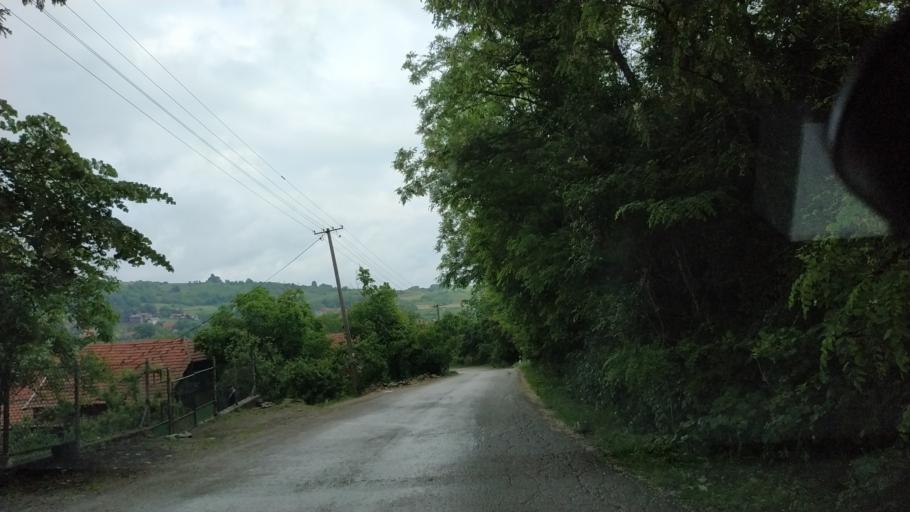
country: RS
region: Central Serbia
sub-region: Toplicki Okrug
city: Prokuplje
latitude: 43.3953
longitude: 21.5543
